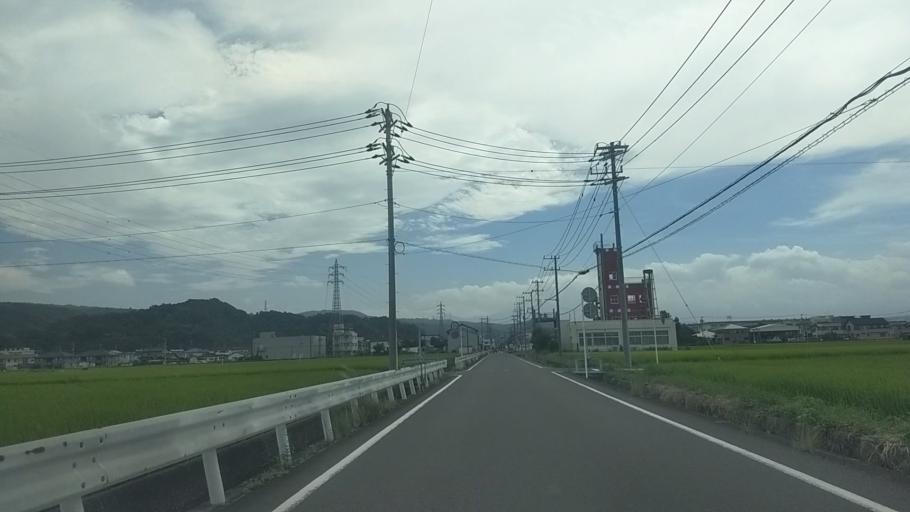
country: JP
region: Shizuoka
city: Mishima
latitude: 35.0605
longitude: 138.9479
